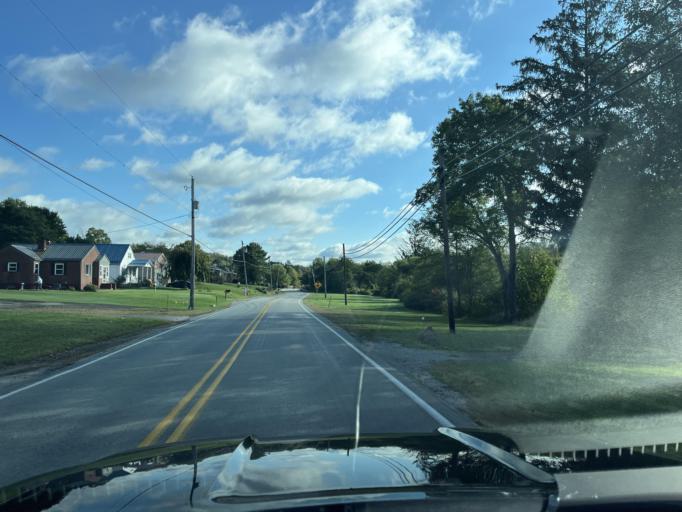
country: US
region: Pennsylvania
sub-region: Fayette County
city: South Uniontown
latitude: 39.8821
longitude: -79.7550
